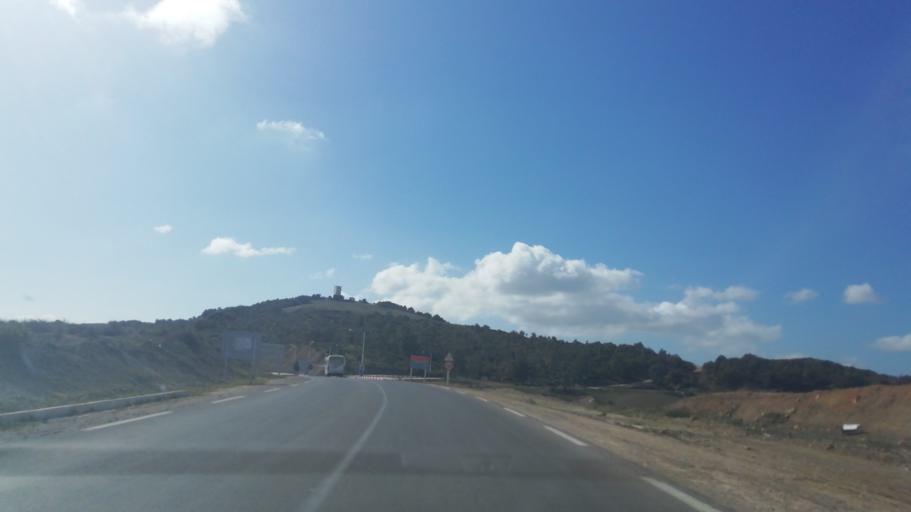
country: DZ
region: Relizane
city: Djidiouia
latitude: 36.0967
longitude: 0.5228
